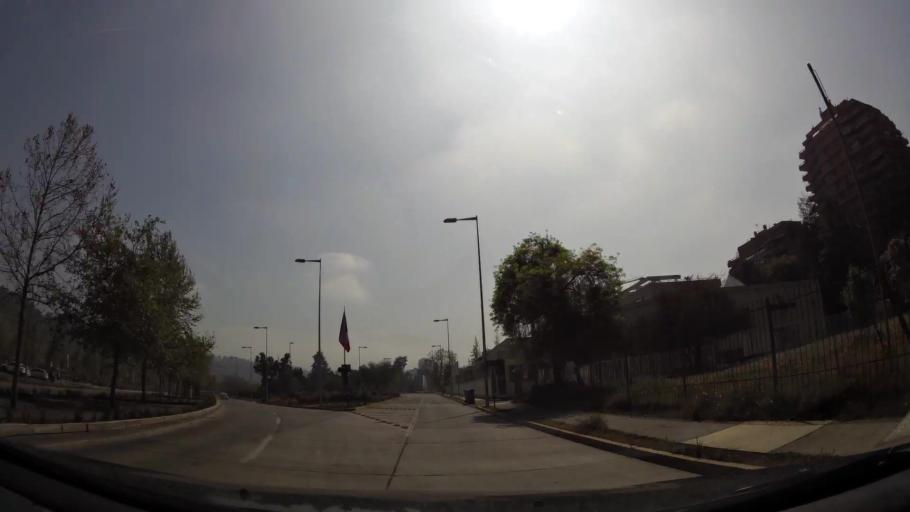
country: CL
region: Santiago Metropolitan
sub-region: Provincia de Santiago
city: Villa Presidente Frei, Nunoa, Santiago, Chile
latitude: -33.4057
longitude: -70.6008
